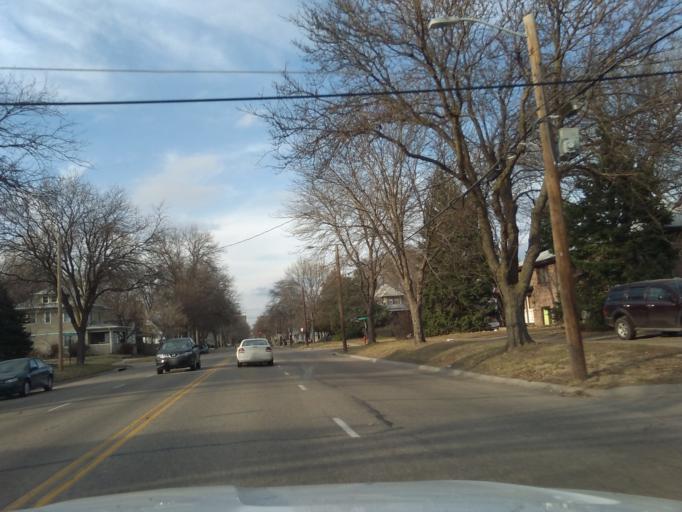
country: US
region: Nebraska
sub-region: Lancaster County
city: Lincoln
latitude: 40.7964
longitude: -96.7027
